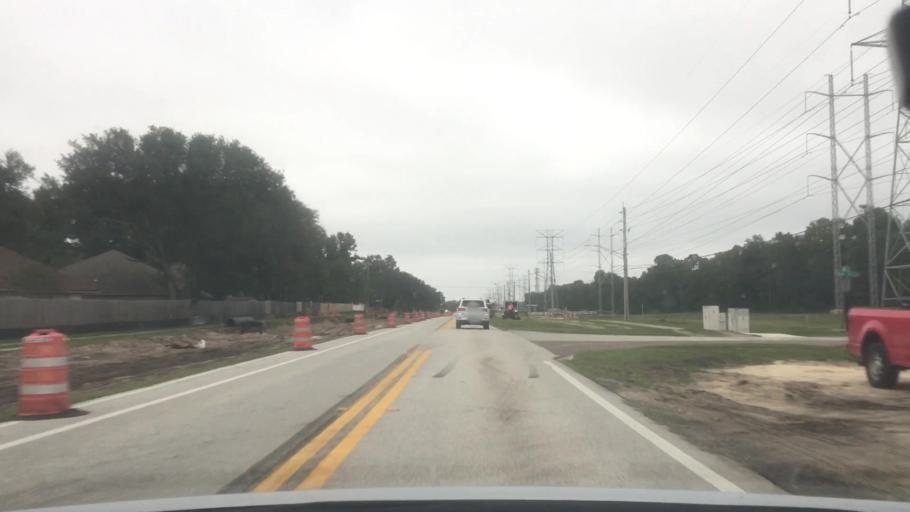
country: US
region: Florida
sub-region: Duval County
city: Atlantic Beach
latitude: 30.3508
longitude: -81.4899
